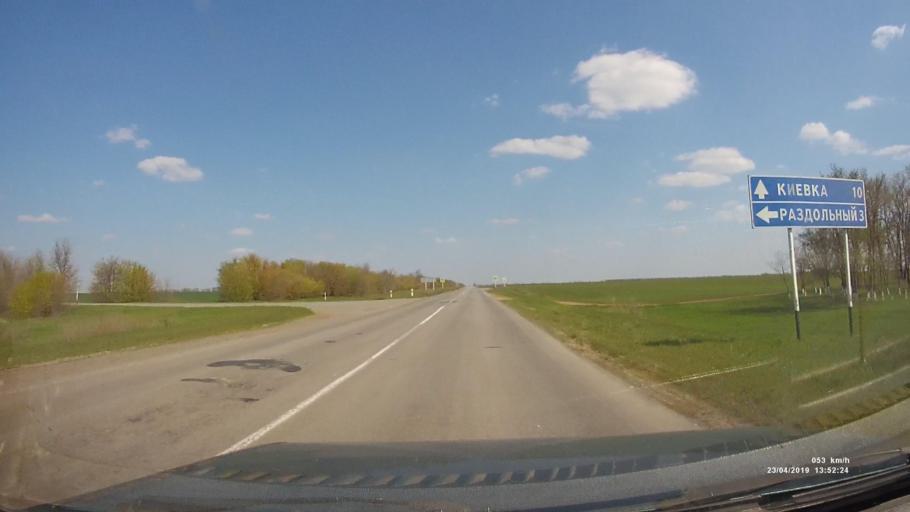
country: RU
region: Rostov
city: Remontnoye
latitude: 46.5995
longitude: 42.9522
